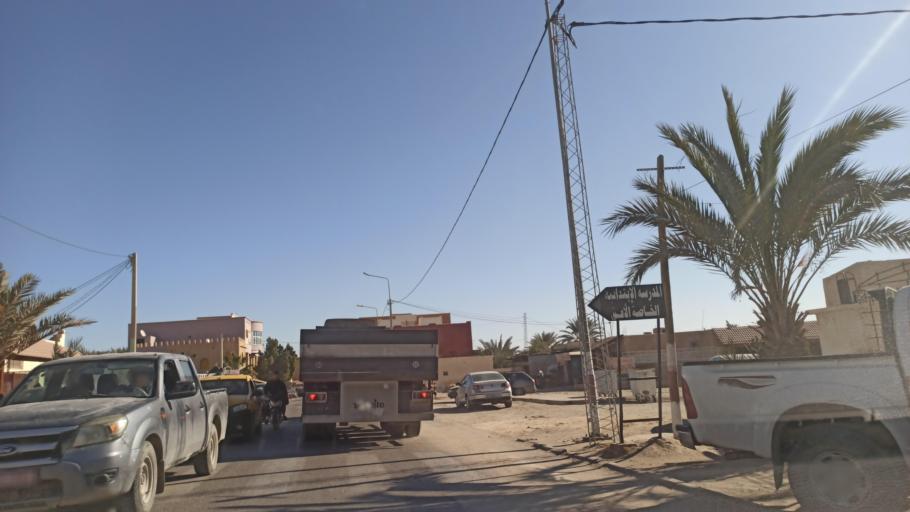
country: TN
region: Gafsa
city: Al Metlaoui
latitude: 34.3146
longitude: 8.4094
